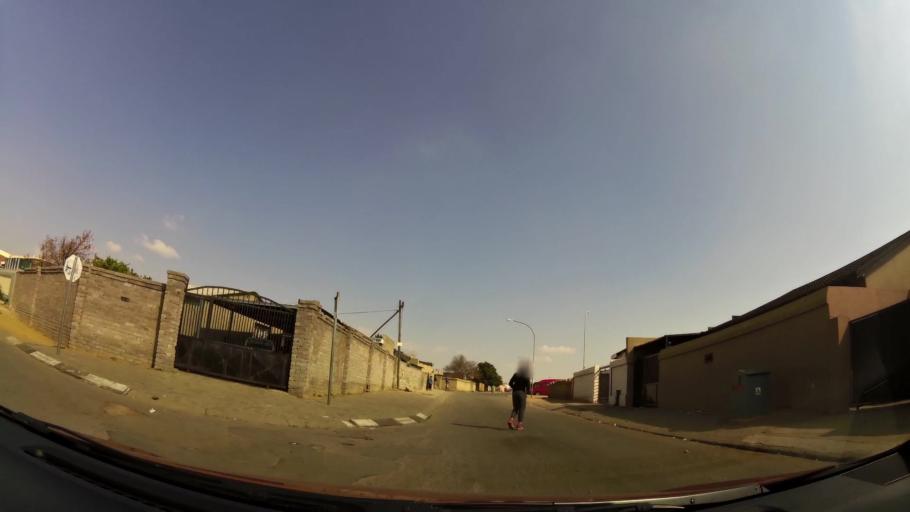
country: ZA
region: Gauteng
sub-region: City of Johannesburg Metropolitan Municipality
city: Johannesburg
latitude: -26.2388
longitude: 27.9547
